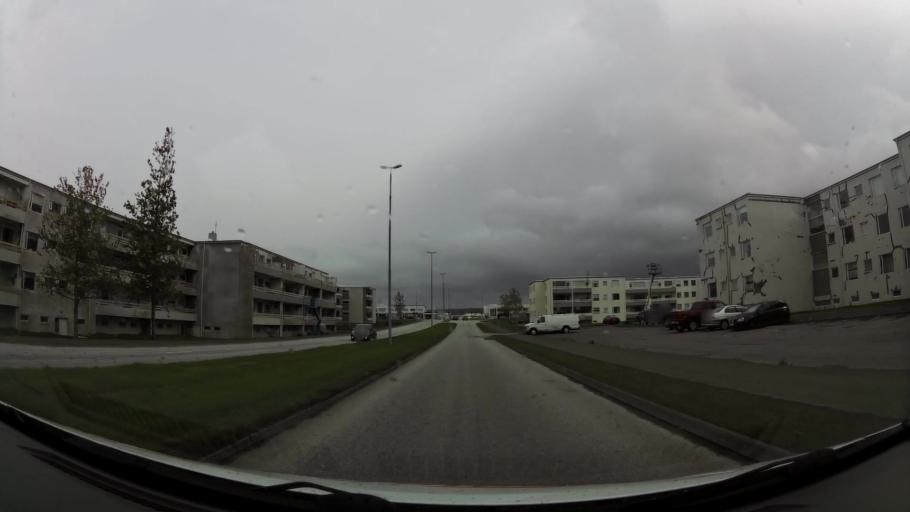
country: IS
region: Capital Region
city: Hafnarfjoerdur
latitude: 64.0789
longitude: -21.9540
